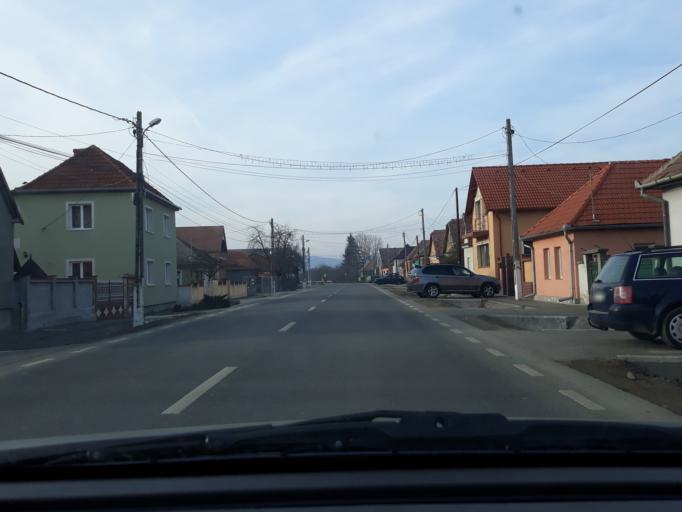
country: RO
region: Salaj
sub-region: Comuna Varsolt
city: Varsolt
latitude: 47.2099
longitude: 22.9094
